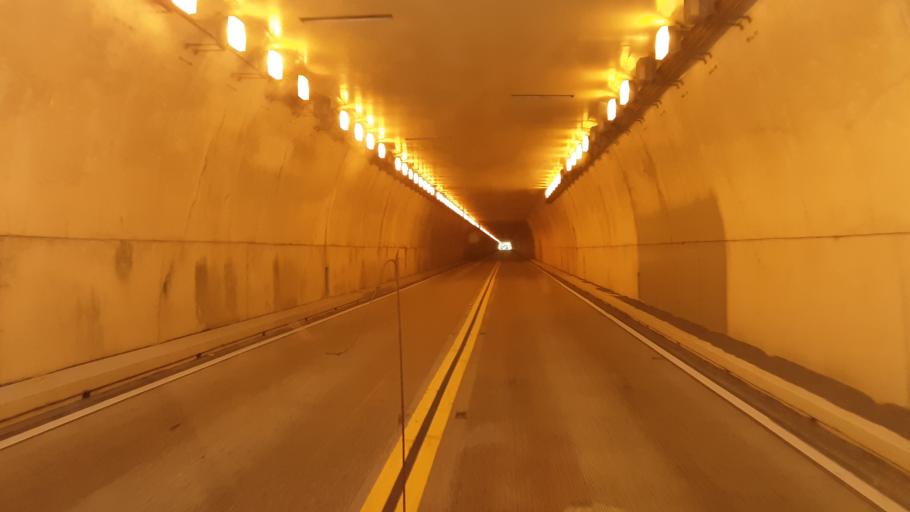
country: US
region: Oregon
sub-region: Josephine County
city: Cave Junction
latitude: 41.9682
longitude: -123.7466
